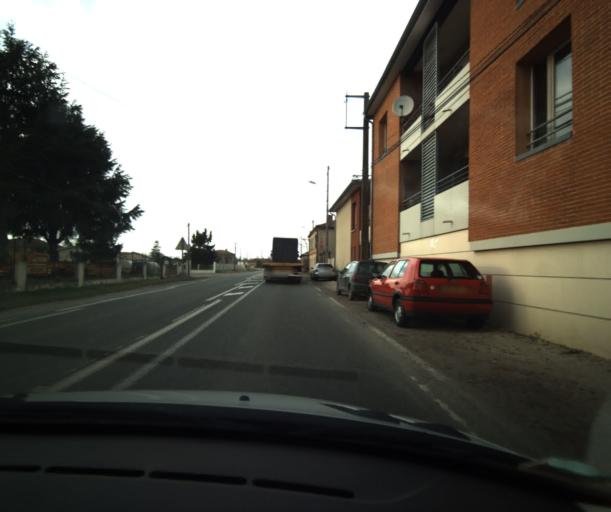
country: FR
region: Midi-Pyrenees
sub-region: Departement du Tarn-et-Garonne
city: Saint-Porquier
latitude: 44.0072
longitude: 1.1767
